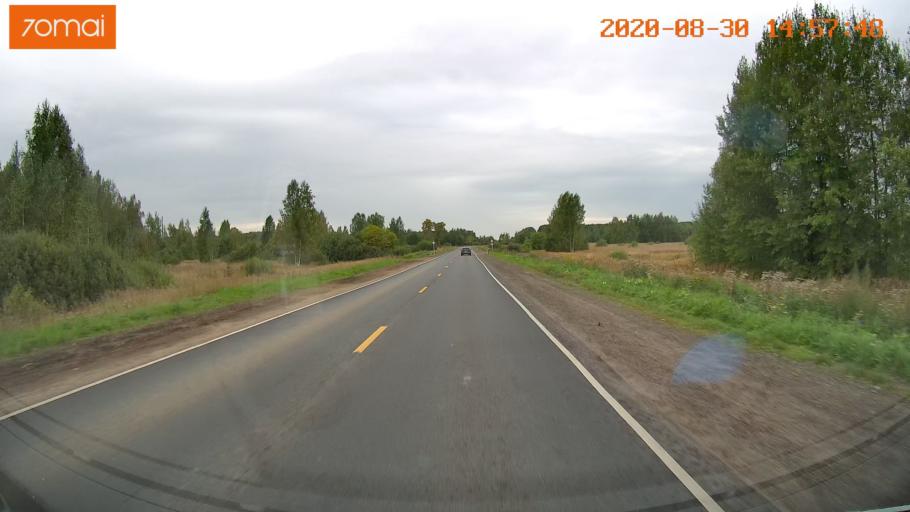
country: RU
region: Ivanovo
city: Navoloki
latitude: 57.3587
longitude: 42.0006
